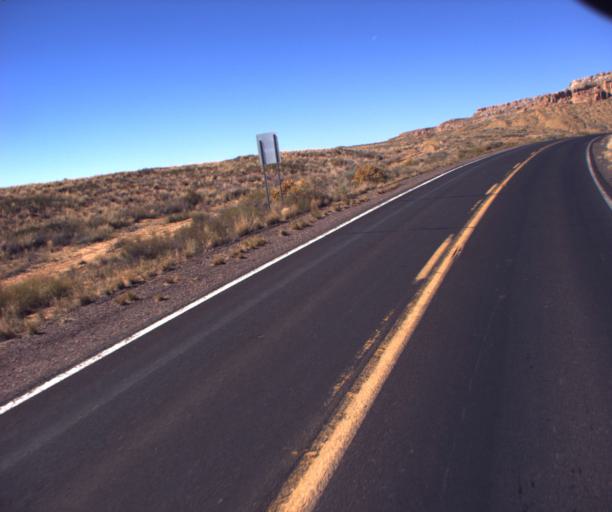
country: US
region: Arizona
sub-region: Navajo County
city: First Mesa
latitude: 35.7945
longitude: -110.5097
